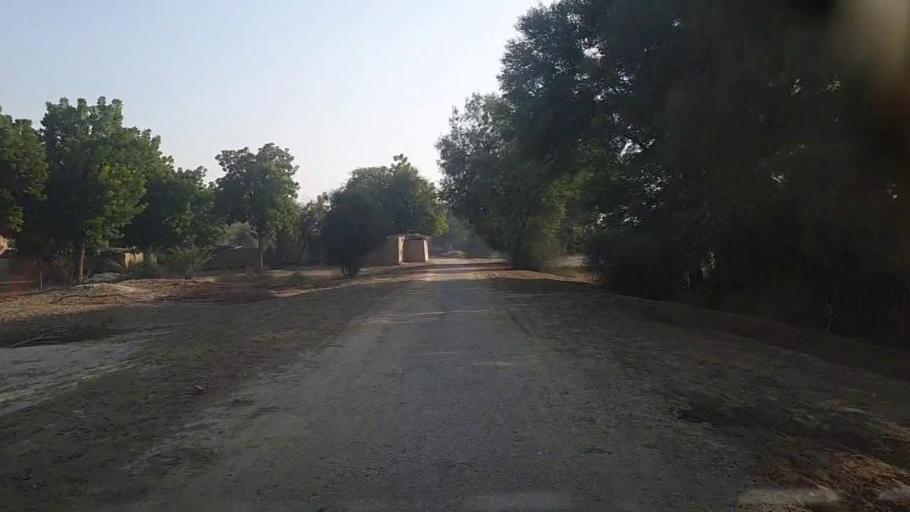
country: PK
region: Sindh
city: Kandiari
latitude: 26.7690
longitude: 68.5119
